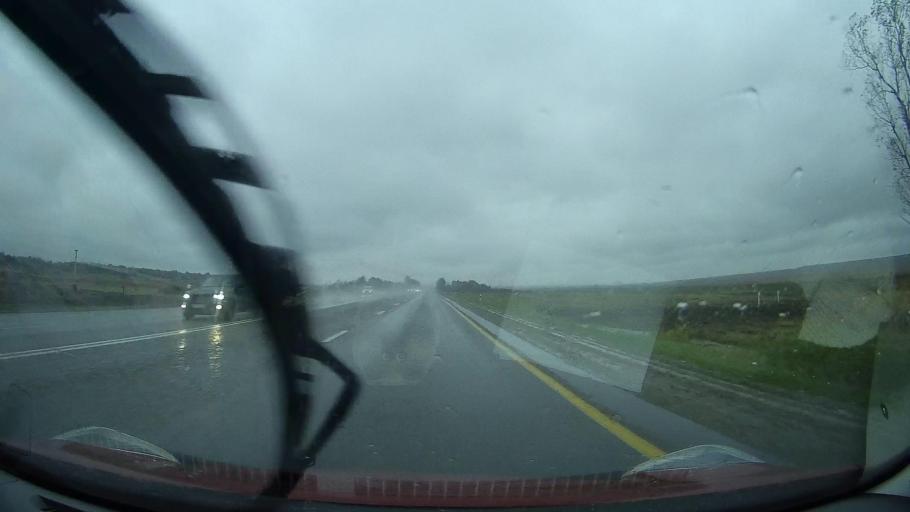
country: RU
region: Stavropol'skiy
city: Nevinnomyssk
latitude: 44.6289
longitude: 42.0388
